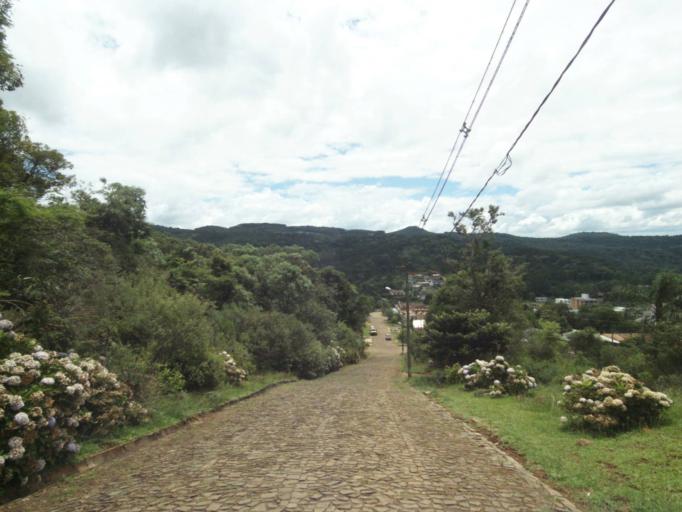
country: BR
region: Parana
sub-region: Pinhao
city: Pinhao
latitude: -26.1606
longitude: -51.5579
